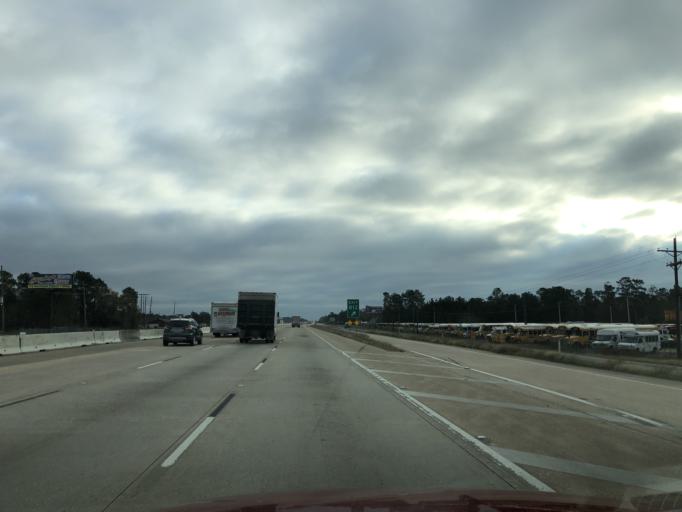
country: US
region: Texas
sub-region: Chambers County
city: Anahuac
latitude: 29.8403
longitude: -94.6626
